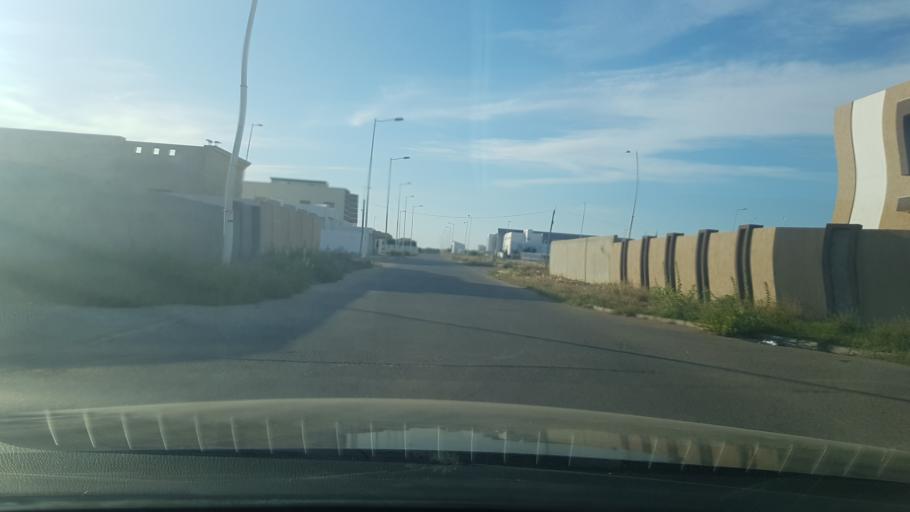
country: TN
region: Safaqis
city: Al Qarmadah
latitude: 34.8347
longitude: 10.7573
